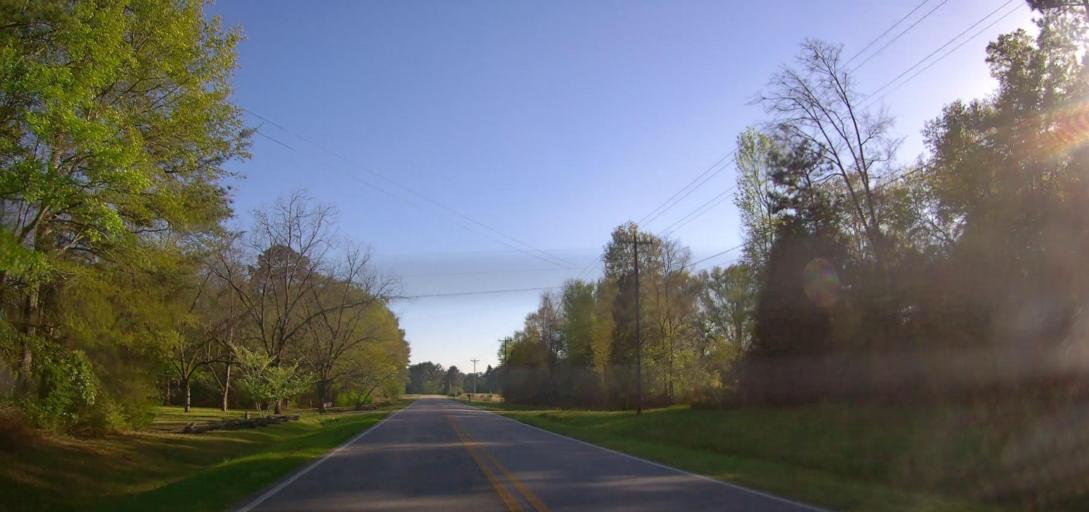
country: US
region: Georgia
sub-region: Butts County
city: Indian Springs
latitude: 33.2848
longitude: -83.8958
